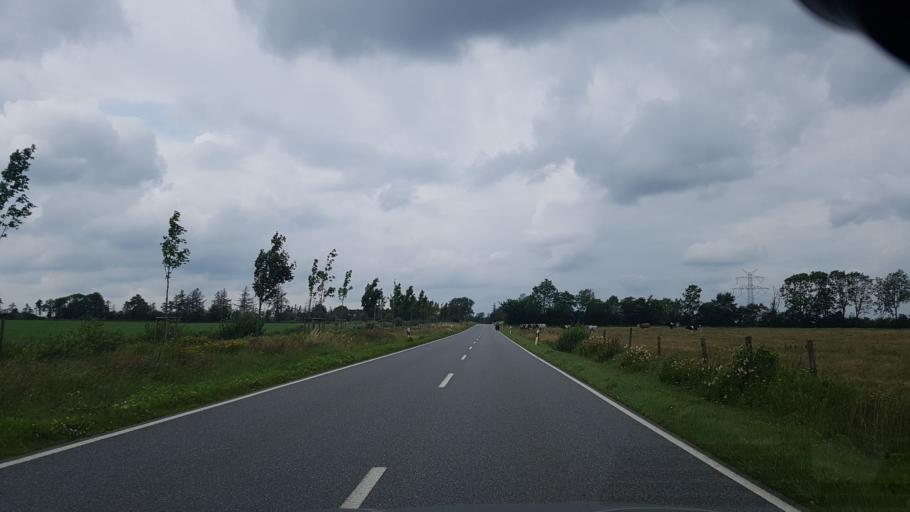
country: DE
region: Schleswig-Holstein
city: Osterby
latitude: 54.8131
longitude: 9.2308
